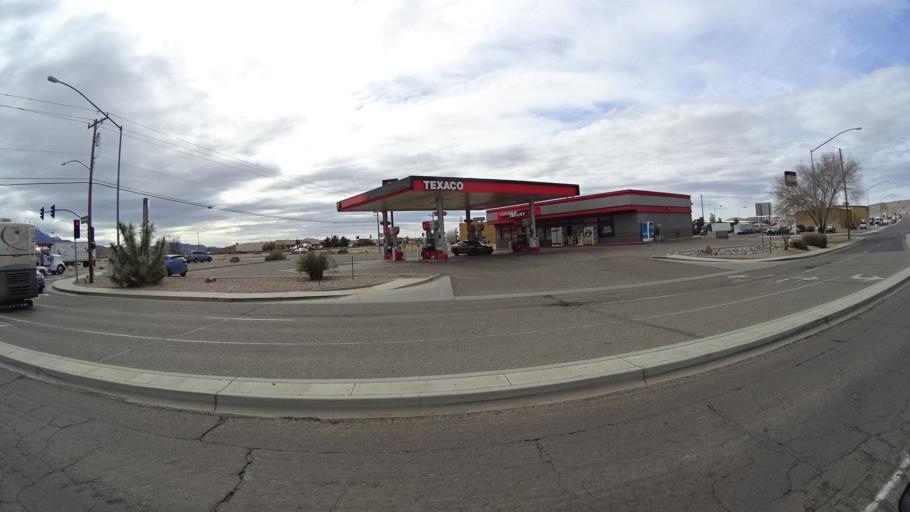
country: US
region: Arizona
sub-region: Mohave County
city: New Kingman-Butler
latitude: 35.2228
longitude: -114.0026
